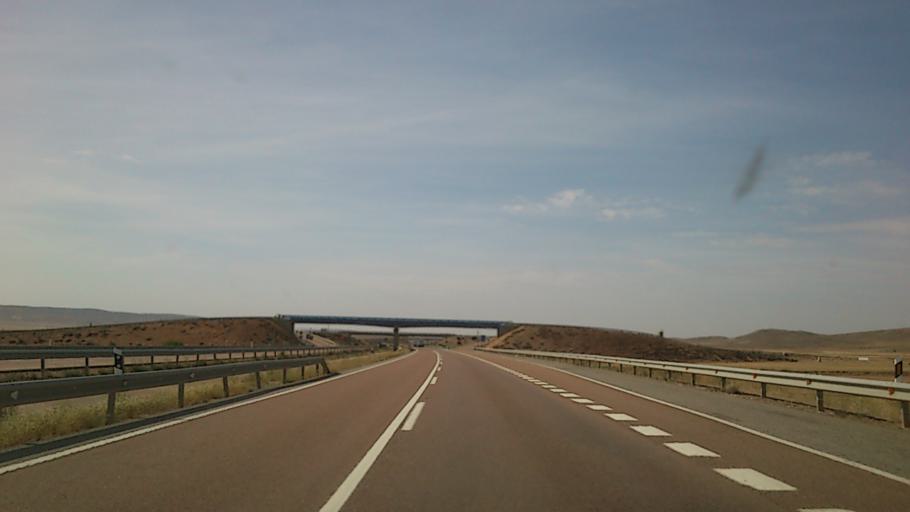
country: ES
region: Aragon
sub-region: Provincia de Teruel
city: Singra
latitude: 40.6179
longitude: -1.2930
